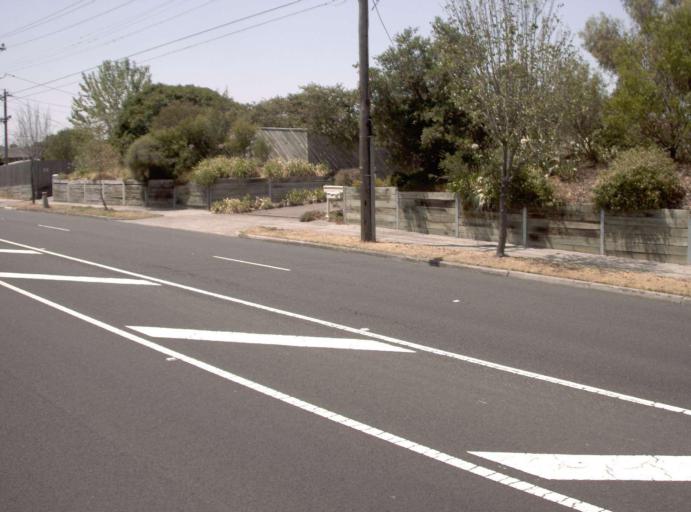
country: AU
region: Victoria
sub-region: Manningham
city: Bulleen
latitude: -37.7776
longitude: 145.0849
